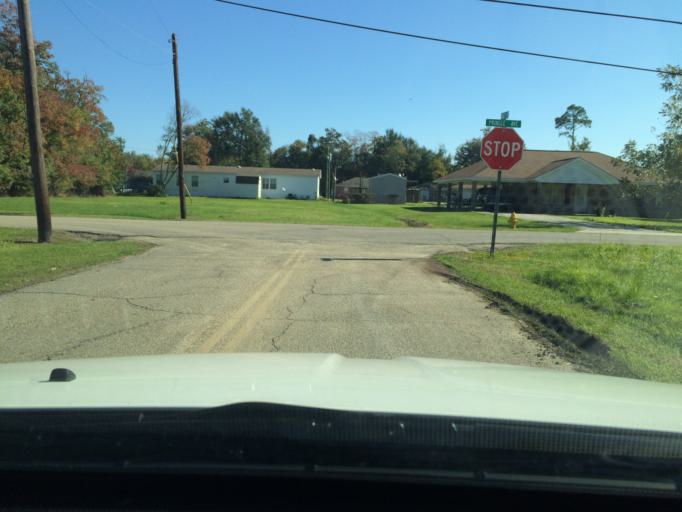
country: US
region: Mississippi
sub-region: Harrison County
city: D'Iberville
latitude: 30.4281
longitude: -88.8880
